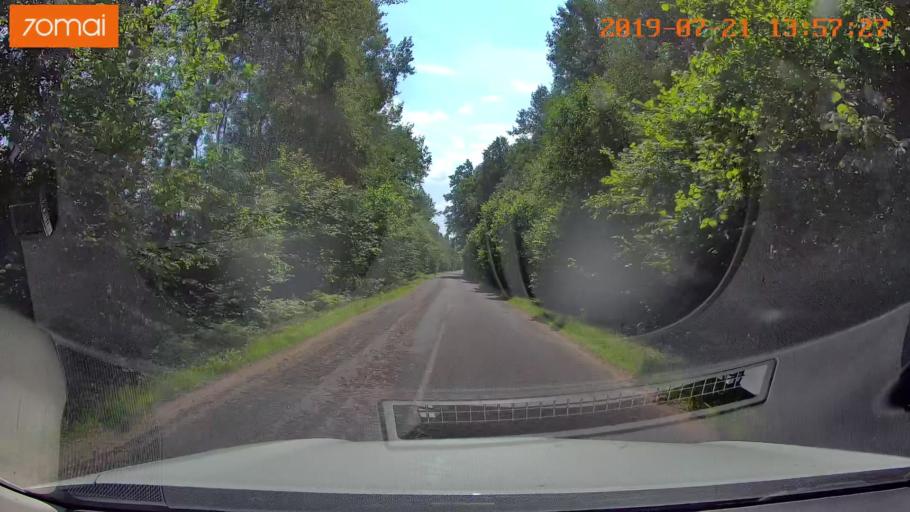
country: BY
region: Grodnenskaya
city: Lyubcha
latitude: 53.7727
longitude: 26.0881
